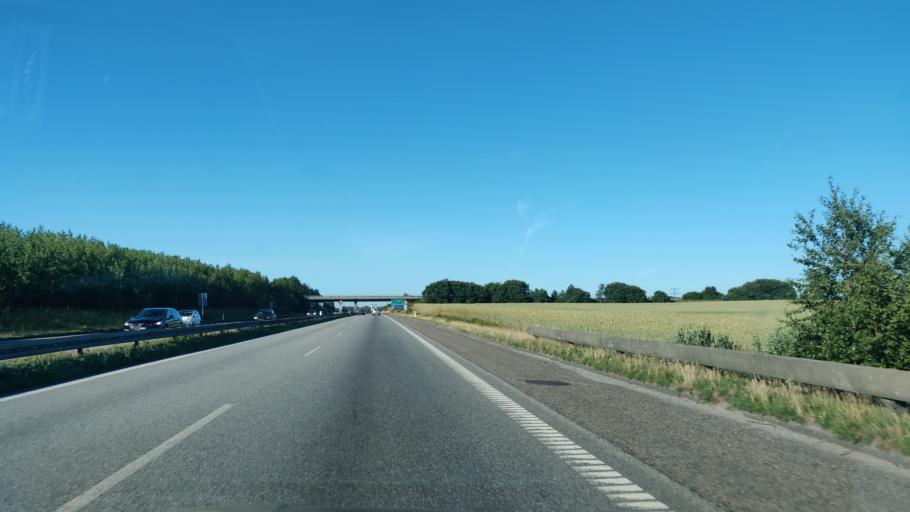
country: DK
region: North Denmark
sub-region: Alborg Kommune
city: Svenstrup
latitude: 56.9428
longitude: 9.8590
